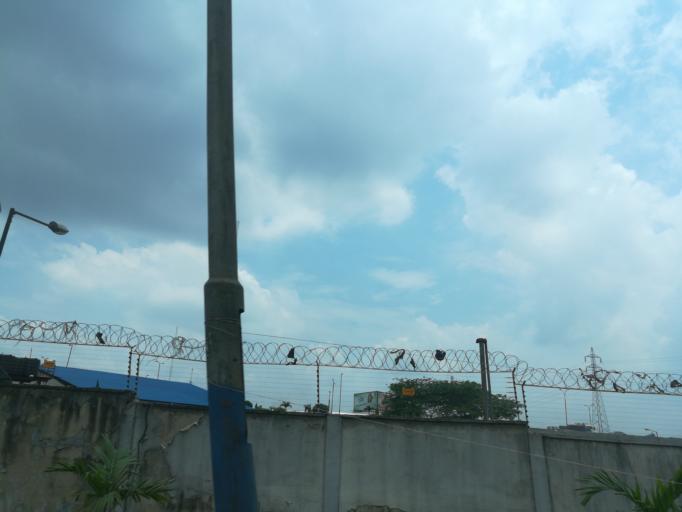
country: NG
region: Lagos
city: Ojota
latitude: 6.5929
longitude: 3.3816
